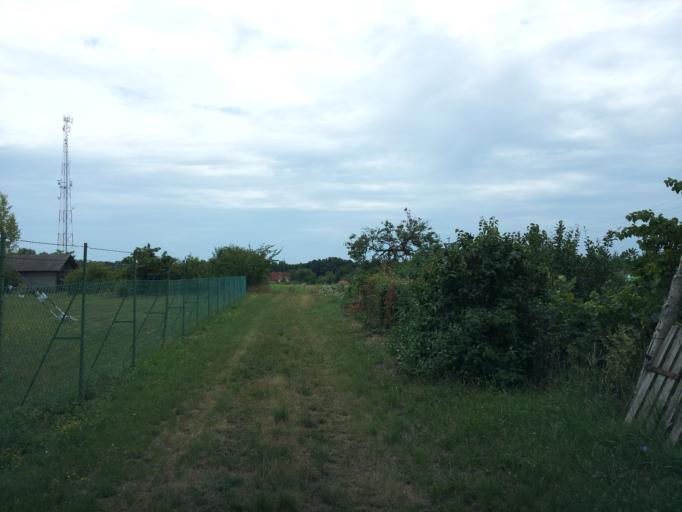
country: HU
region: Vas
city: Vasvar
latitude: 47.0512
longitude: 16.8122
